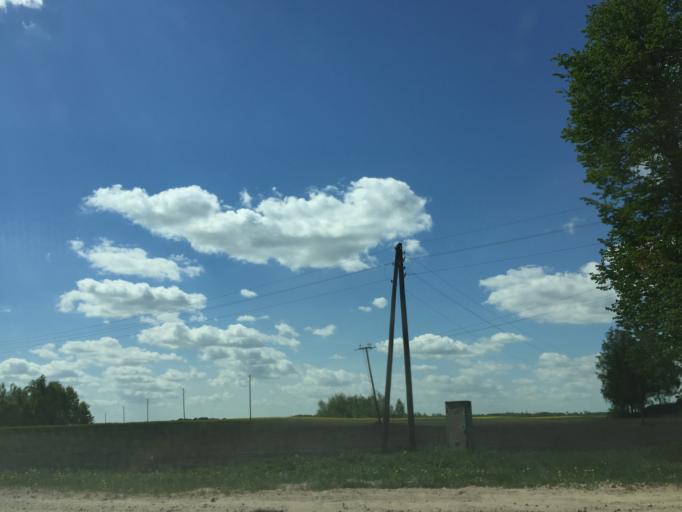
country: LV
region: Bauskas Rajons
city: Bauska
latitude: 56.4956
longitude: 24.1241
